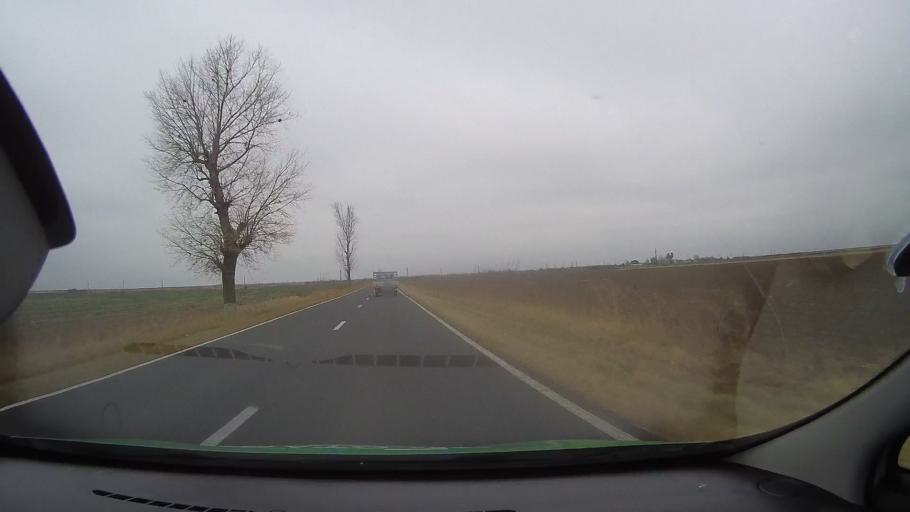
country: RO
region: Ialomita
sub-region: Comuna Scanteia
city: Iazu
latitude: 44.7386
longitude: 27.4367
